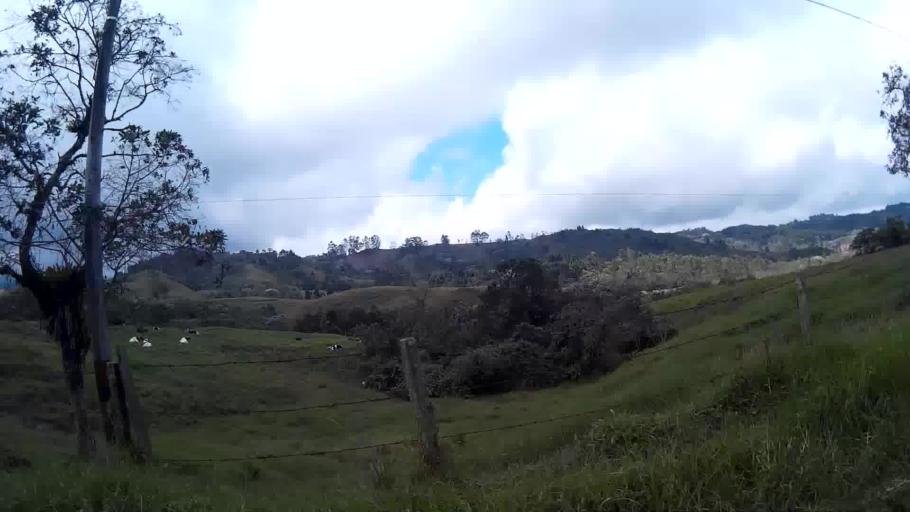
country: CO
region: Quindio
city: Filandia
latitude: 4.6877
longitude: -75.6144
